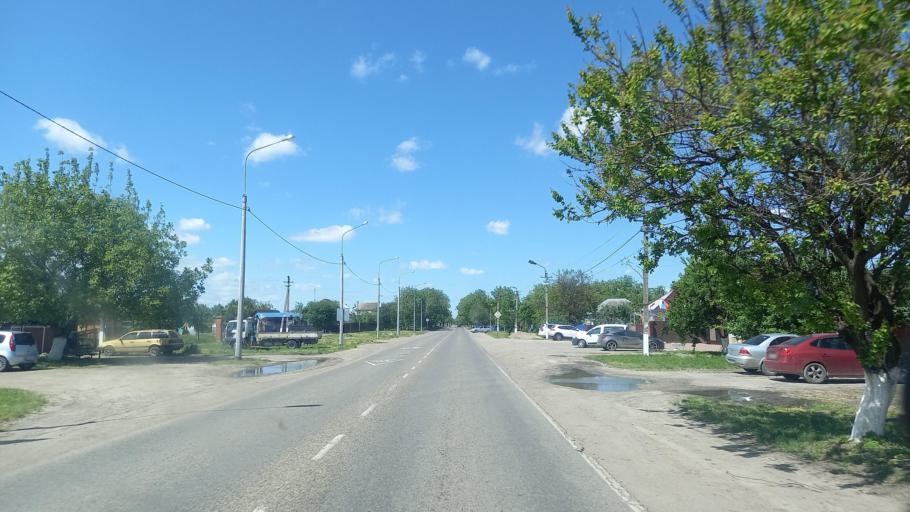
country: RU
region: Krasnodarskiy
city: Novoukrainskoye
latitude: 45.3803
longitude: 40.5221
